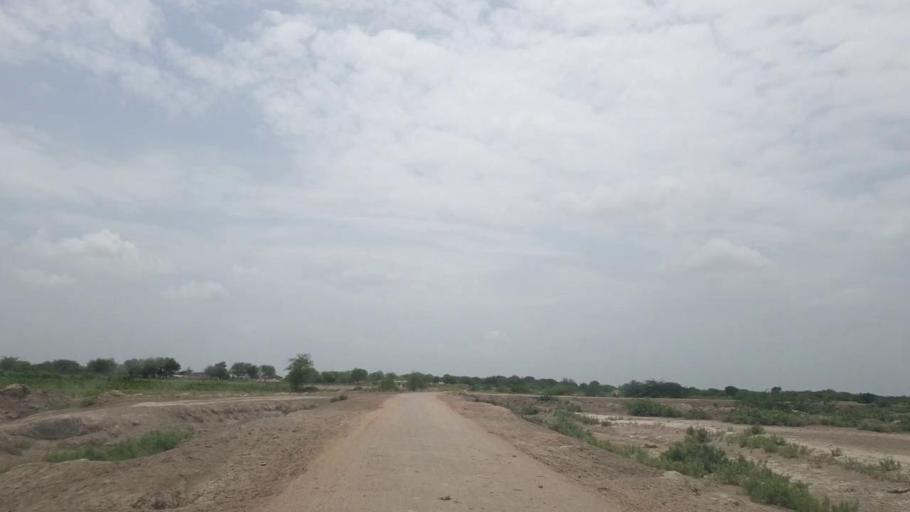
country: PK
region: Sindh
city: Naukot
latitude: 24.9342
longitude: 69.1831
